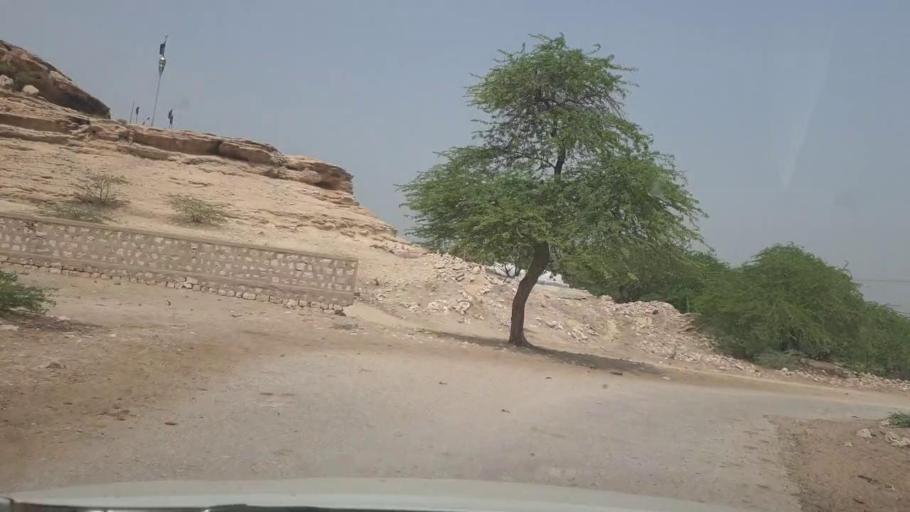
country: PK
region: Sindh
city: Kot Diji
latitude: 27.3488
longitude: 68.7176
